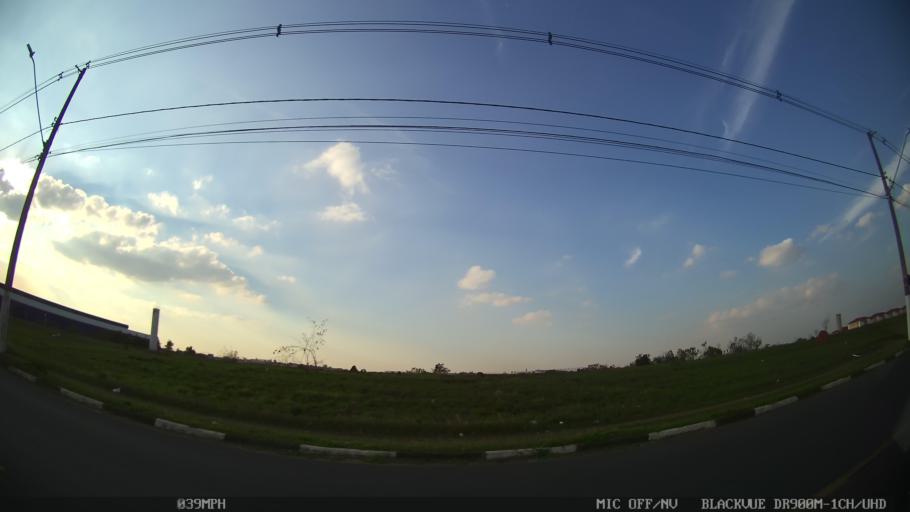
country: BR
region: Sao Paulo
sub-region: Hortolandia
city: Hortolandia
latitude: -22.8760
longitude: -47.1762
